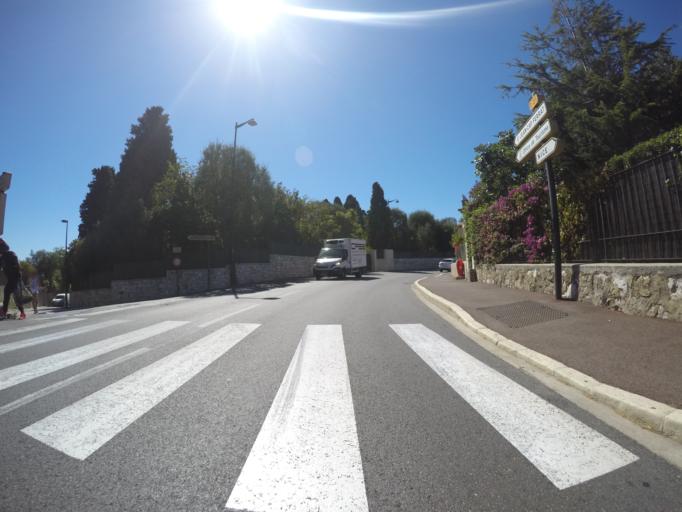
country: FR
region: Provence-Alpes-Cote d'Azur
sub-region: Departement des Alpes-Maritimes
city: Saint-Jean-Cap-Ferrat
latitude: 43.6941
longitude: 7.3288
